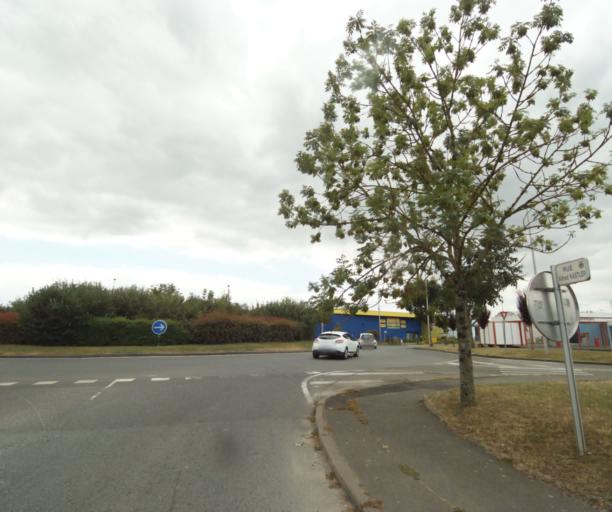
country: FR
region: Centre
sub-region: Departement du Loiret
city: Checy
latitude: 47.9061
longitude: 2.0364
